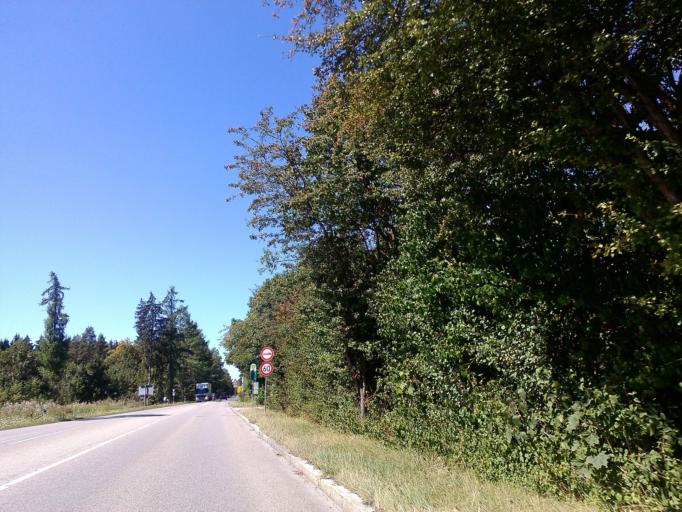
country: DE
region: Bavaria
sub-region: Upper Bavaria
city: Krailling
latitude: 48.0972
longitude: 11.3733
